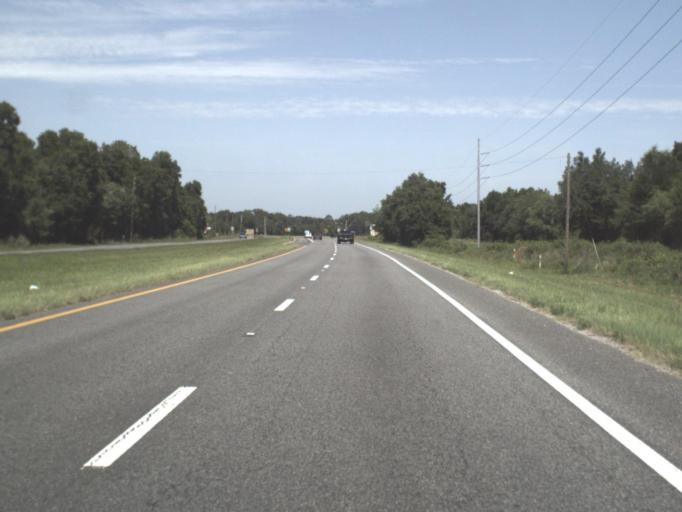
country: US
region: Florida
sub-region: Dixie County
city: Cross City
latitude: 29.6097
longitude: -83.0775
